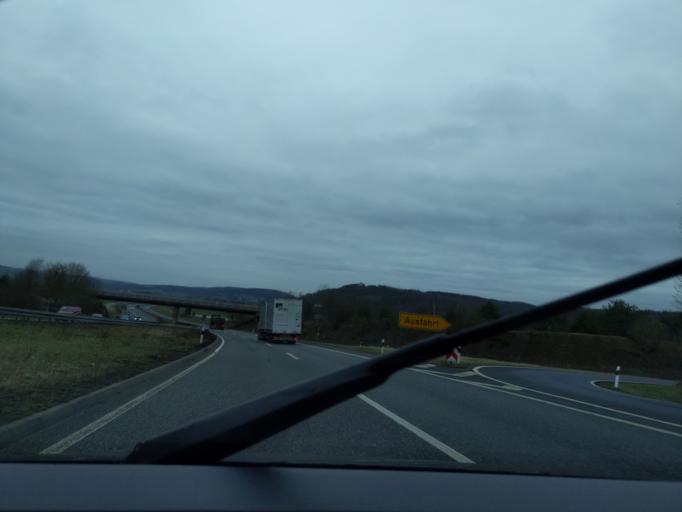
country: DE
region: Hesse
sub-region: Regierungsbezirk Giessen
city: Fronhausen
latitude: 50.7241
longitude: 8.7367
